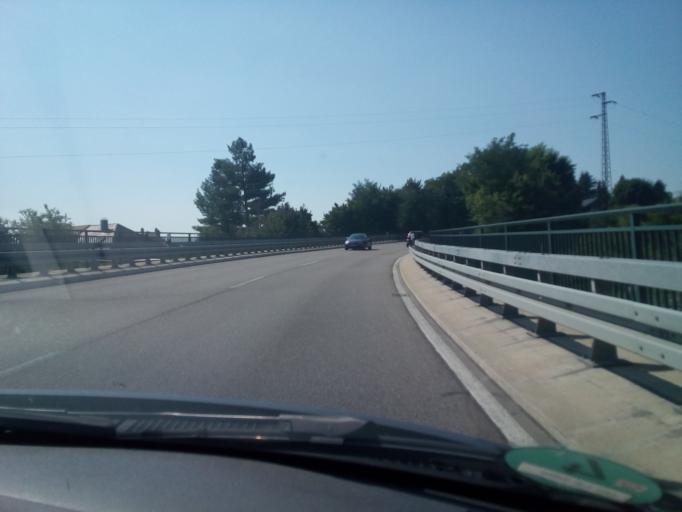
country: DE
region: Baden-Wuerttemberg
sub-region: Karlsruhe Region
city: Buhl
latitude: 48.6971
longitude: 8.1505
